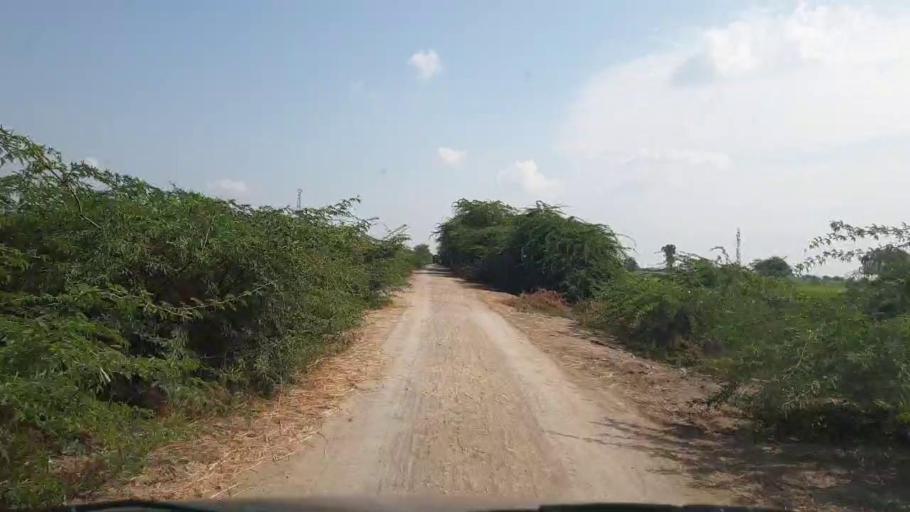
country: PK
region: Sindh
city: Badin
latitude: 24.4658
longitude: 68.5739
